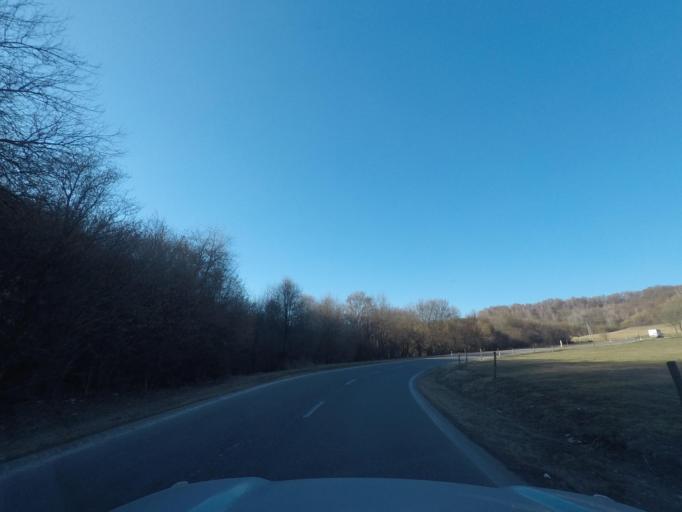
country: SK
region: Presovsky
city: Medzilaborce
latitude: 49.1749
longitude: 22.0236
